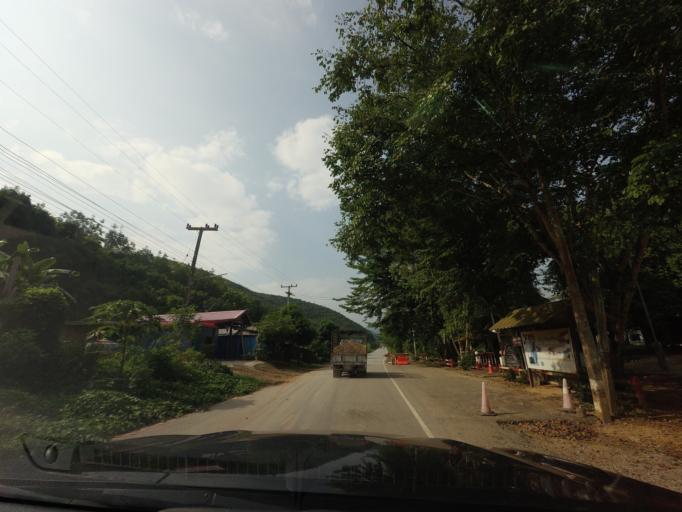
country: TH
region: Loei
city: Chiang Khan
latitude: 17.8405
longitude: 101.5679
